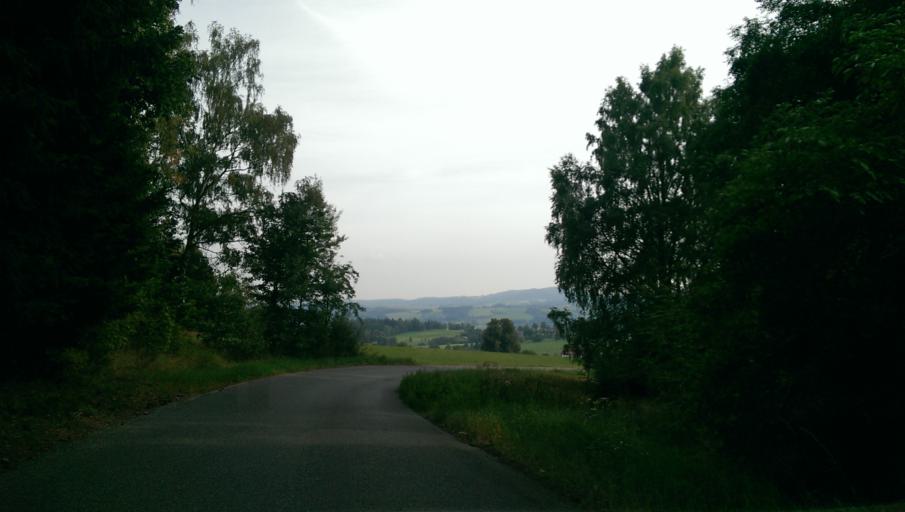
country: CZ
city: Pencin
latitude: 50.6628
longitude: 15.2377
